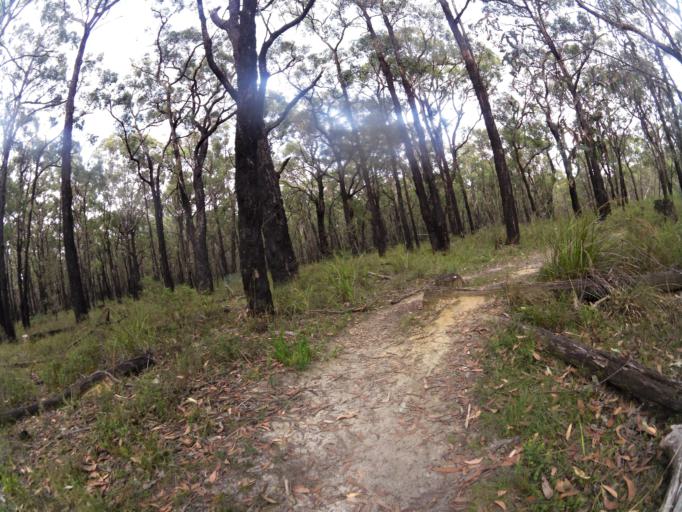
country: AU
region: Victoria
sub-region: Colac-Otway
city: Colac
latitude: -38.4963
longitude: 143.7144
